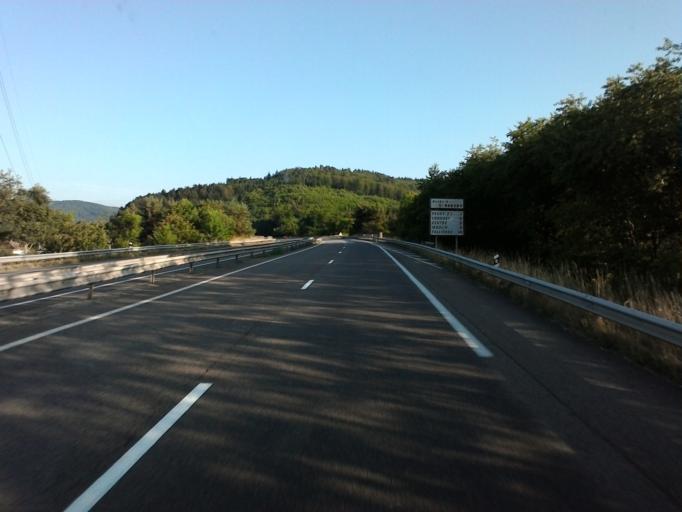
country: FR
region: Lorraine
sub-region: Departement des Vosges
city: Eloyes
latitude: 48.0977
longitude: 6.5898
